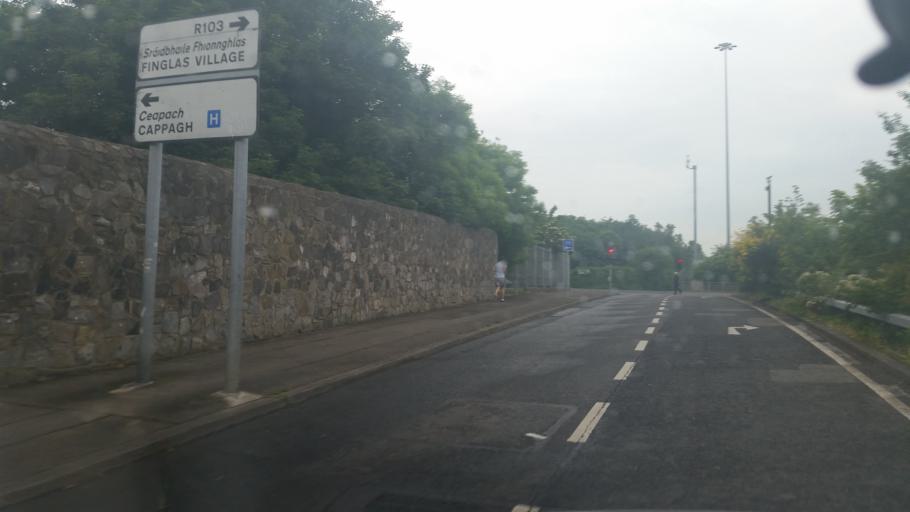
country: IE
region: Leinster
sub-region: Dublin City
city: Finglas
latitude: 53.3894
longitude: -6.3011
